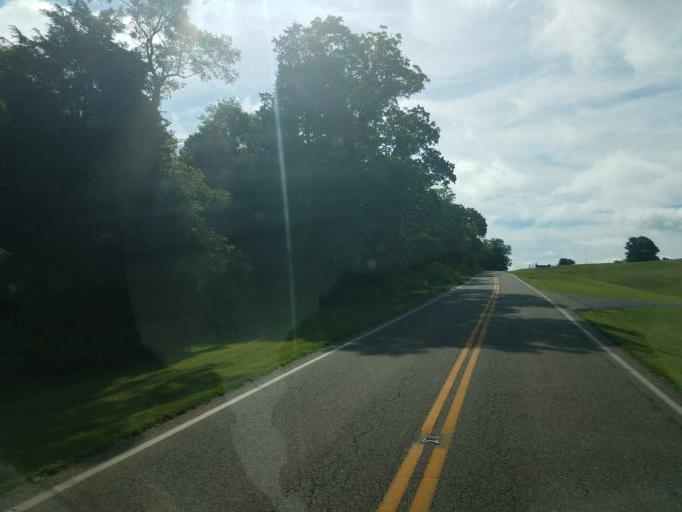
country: US
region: Ohio
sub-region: Gallia County
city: Gallipolis
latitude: 38.8338
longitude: -82.2769
